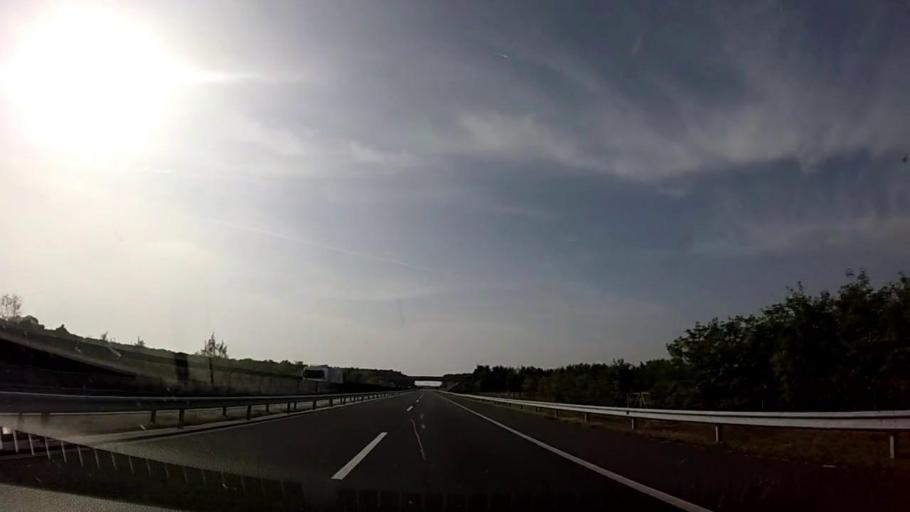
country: HU
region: Somogy
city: Balatonbereny
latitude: 46.6386
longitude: 17.2849
